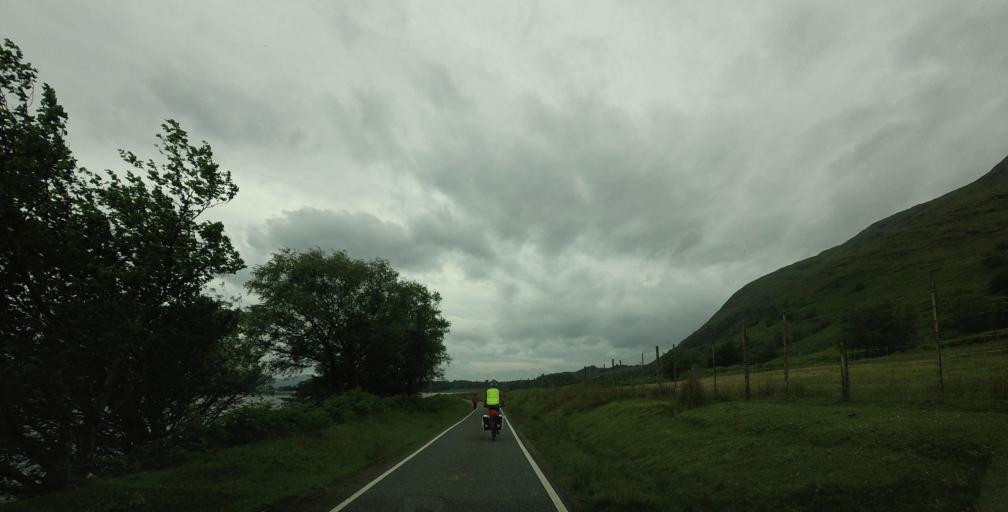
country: GB
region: Scotland
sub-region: Highland
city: Fort William
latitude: 56.7419
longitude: -5.2468
